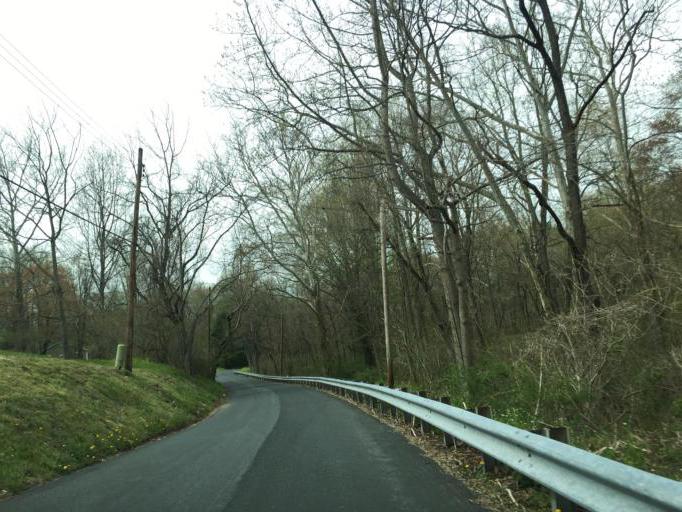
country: US
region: Maryland
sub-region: Baltimore County
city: Hunt Valley
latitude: 39.5622
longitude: -76.6088
